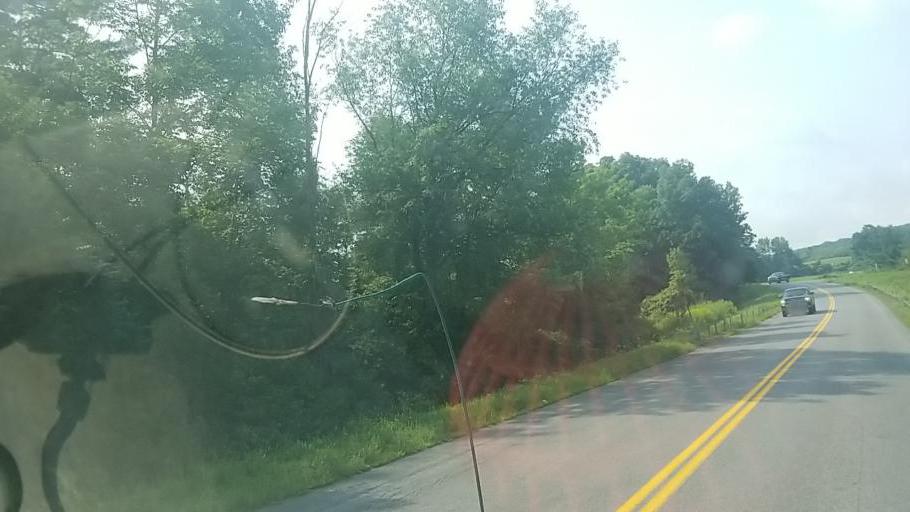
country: US
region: New York
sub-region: Montgomery County
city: Fonda
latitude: 42.9887
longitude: -74.4468
